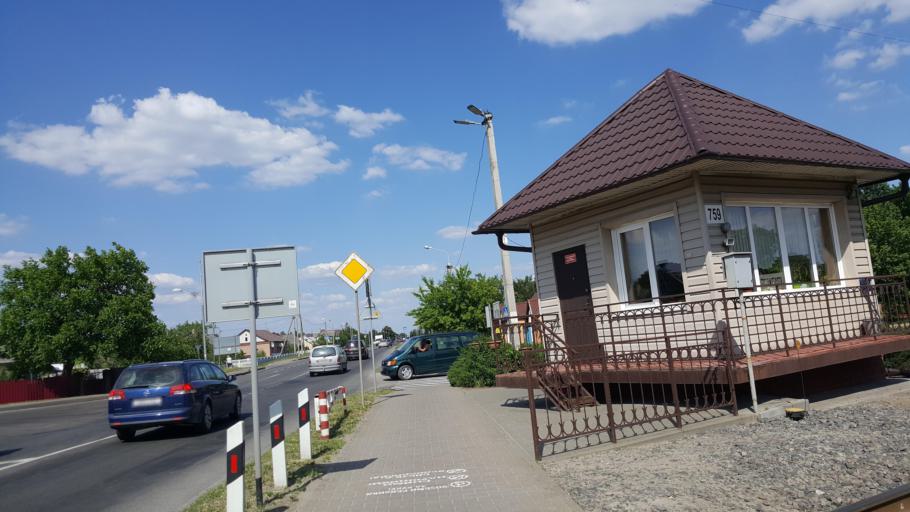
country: BY
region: Brest
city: Horad Kobryn
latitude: 52.2214
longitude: 24.3646
